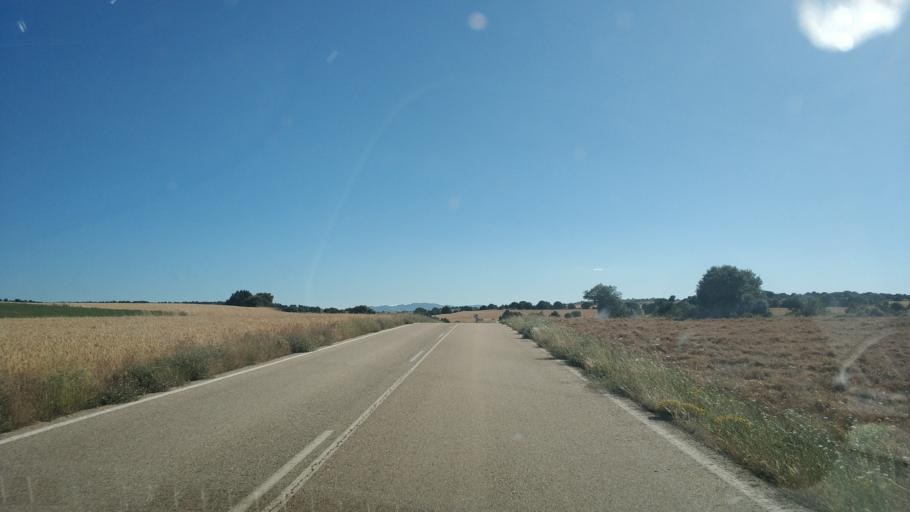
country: ES
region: Castille and Leon
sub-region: Provincia de Soria
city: San Esteban de Gormaz
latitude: 41.4945
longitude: -3.2030
